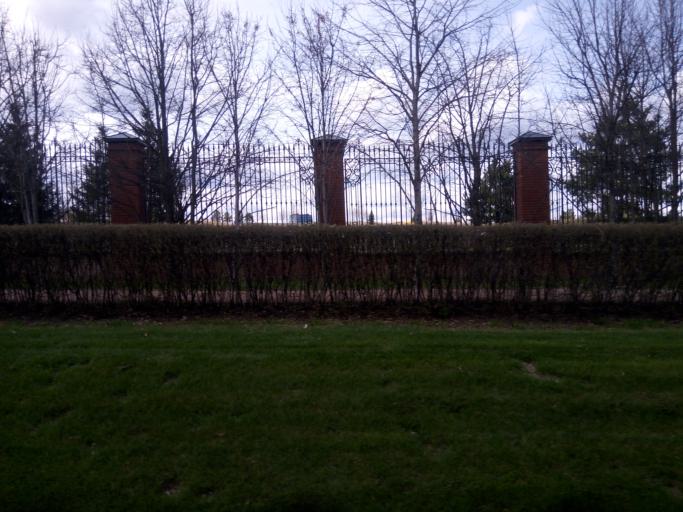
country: RU
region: Moskovskaya
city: Skolkovo
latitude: 55.6905
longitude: 37.3774
